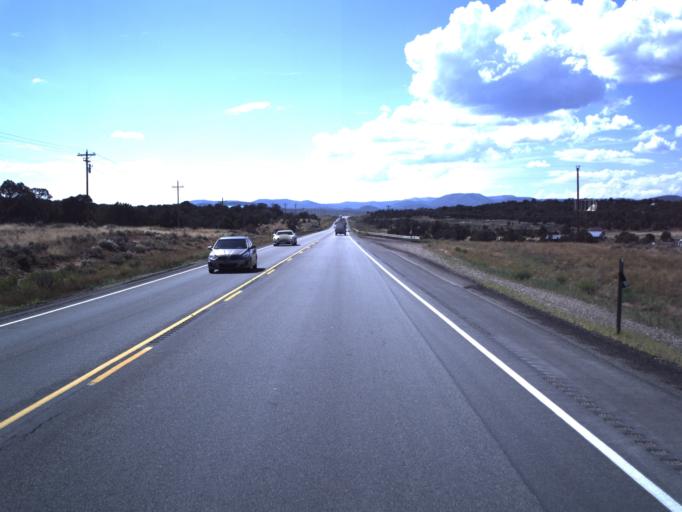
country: US
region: Utah
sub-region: Duchesne County
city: Duchesne
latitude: 40.2066
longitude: -110.8114
